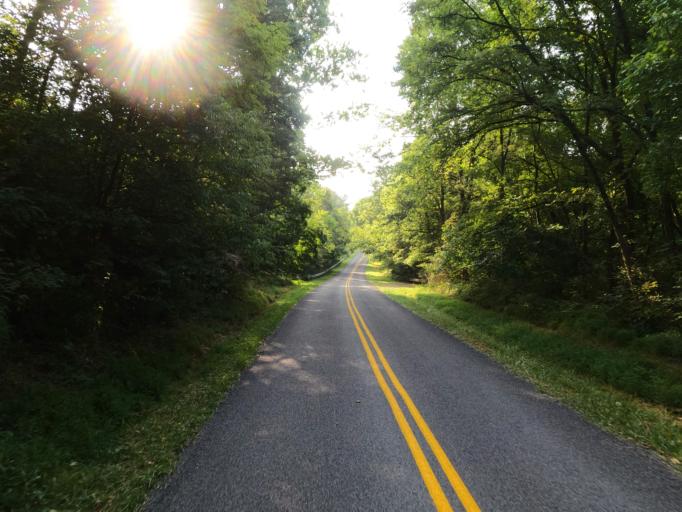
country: US
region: West Virginia
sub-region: Morgan County
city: Berkeley Springs
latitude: 39.6324
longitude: -78.3095
